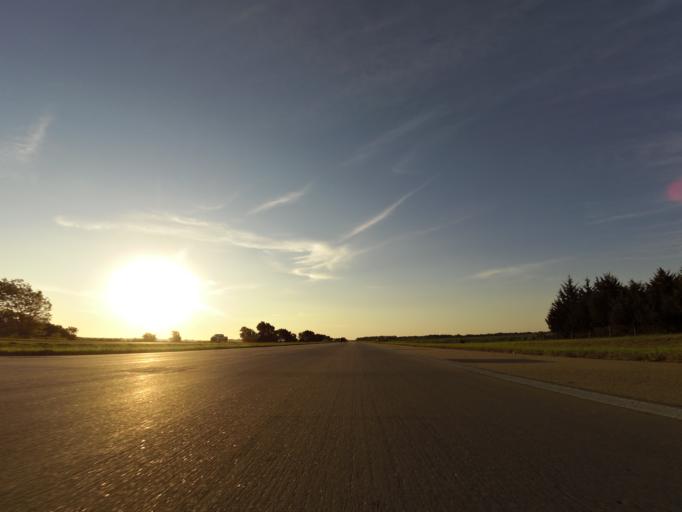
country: US
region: Kansas
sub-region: Reno County
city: Haven
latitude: 37.8897
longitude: -97.7502
